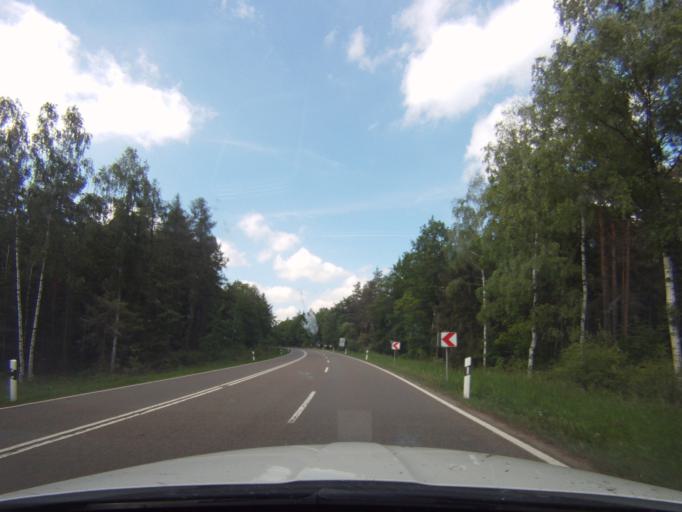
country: DE
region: Thuringia
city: Renthendorf
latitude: 50.7949
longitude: 11.9735
